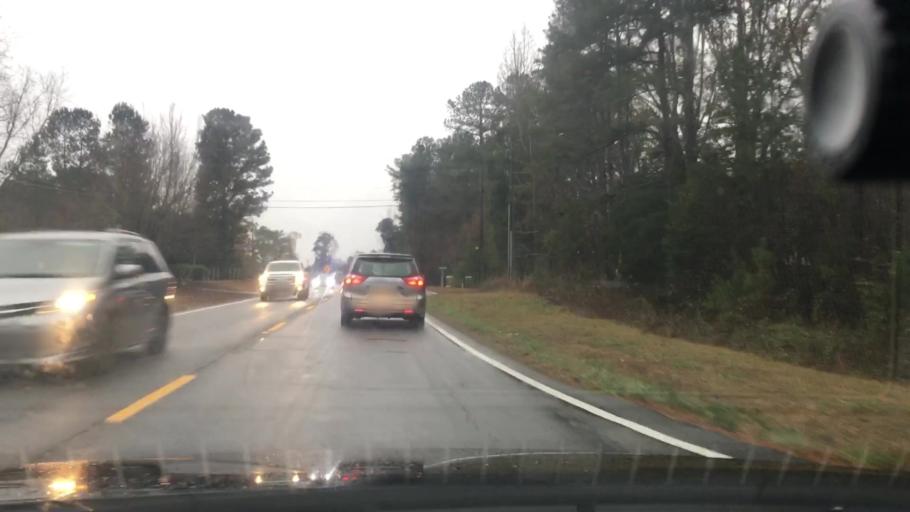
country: US
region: Georgia
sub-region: Fayette County
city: Peachtree City
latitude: 33.3646
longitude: -84.6626
